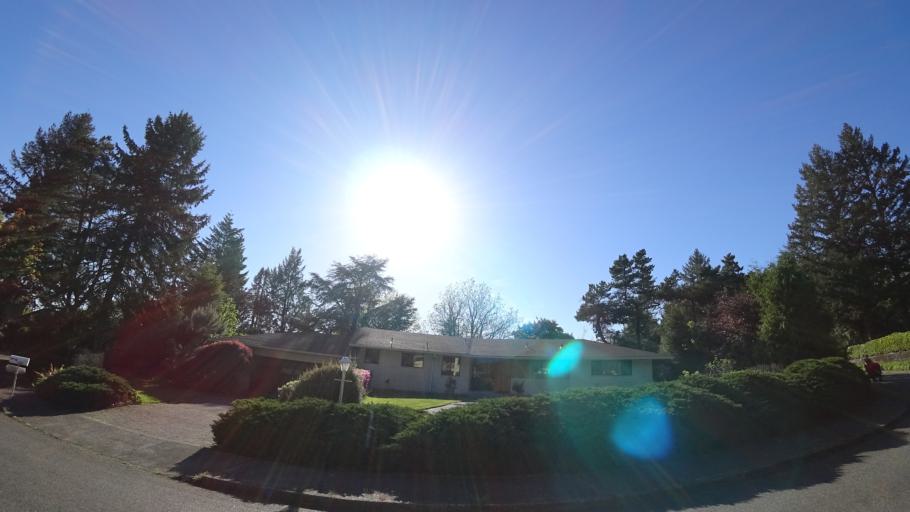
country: US
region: Oregon
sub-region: Washington County
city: West Slope
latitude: 45.5003
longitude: -122.7574
